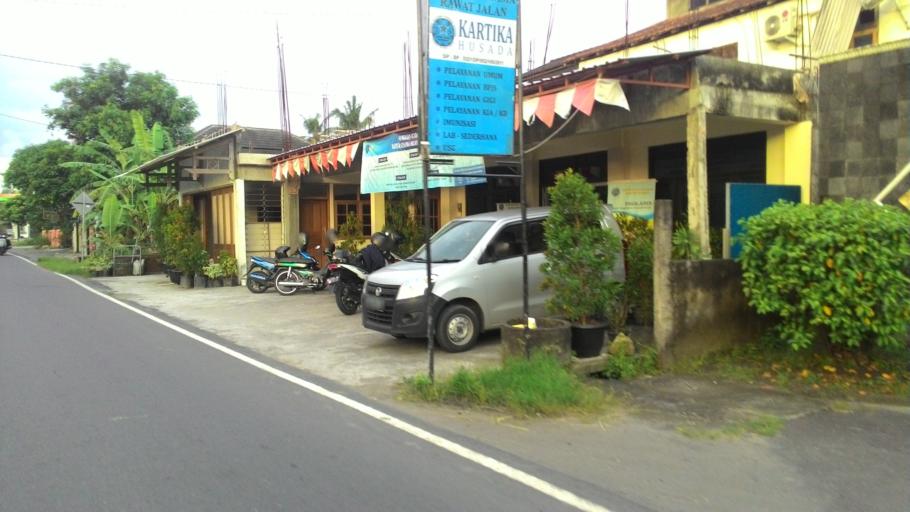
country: ID
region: Daerah Istimewa Yogyakarta
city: Depok
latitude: -7.8308
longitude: 110.4424
